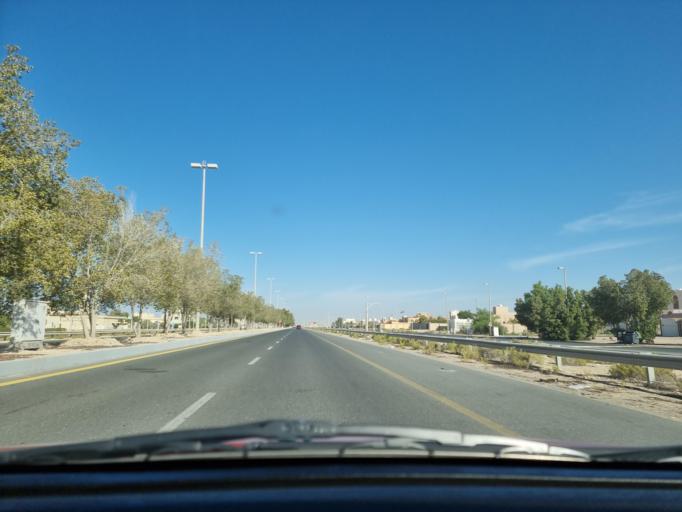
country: AE
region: Abu Dhabi
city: Abu Dhabi
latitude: 24.3894
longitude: 54.6950
